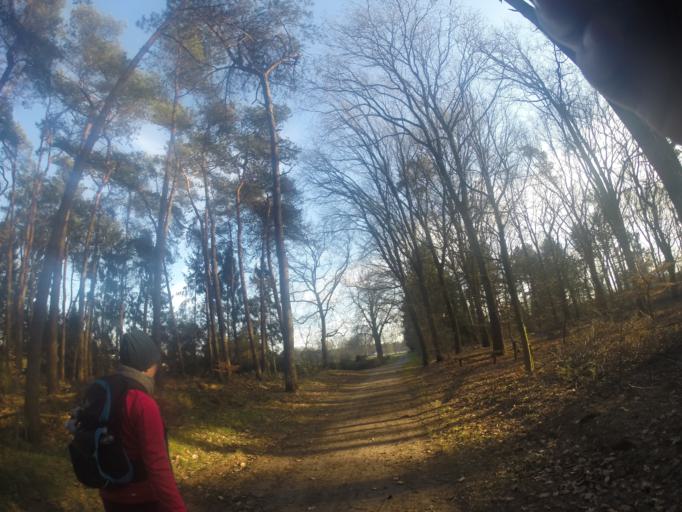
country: NL
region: Gelderland
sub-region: Gemeente Lochem
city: Lochem
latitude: 52.1287
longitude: 6.3573
